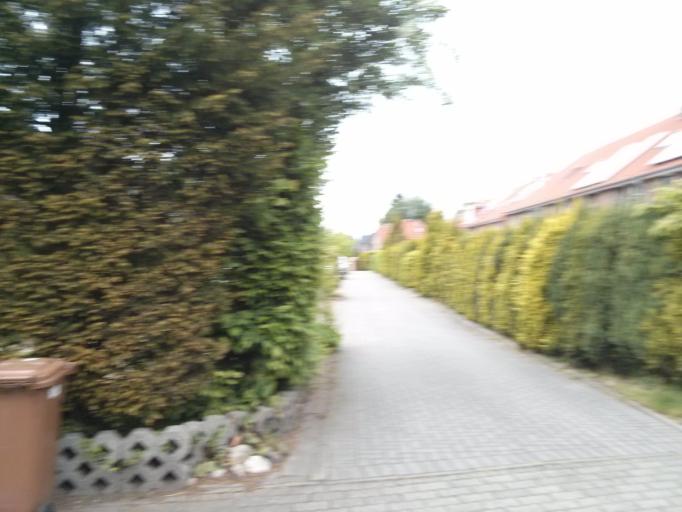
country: DE
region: Schleswig-Holstein
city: Halstenbek
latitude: 53.6295
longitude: 9.8575
